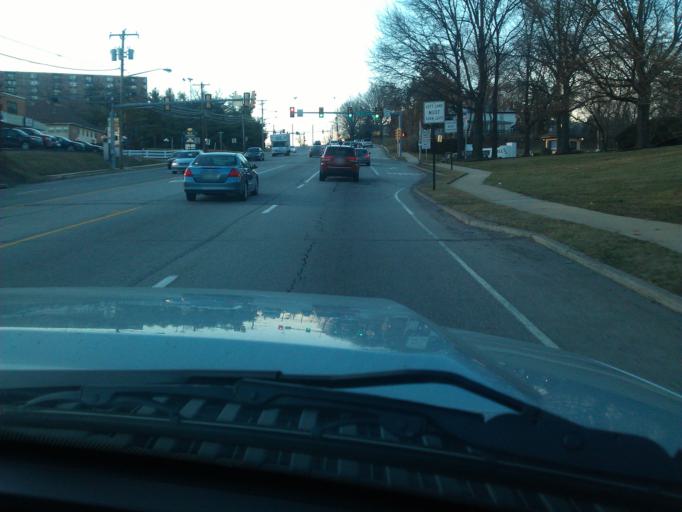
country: US
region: Pennsylvania
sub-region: Montgomery County
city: Plymouth Meeting
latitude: 40.1195
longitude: -75.2868
